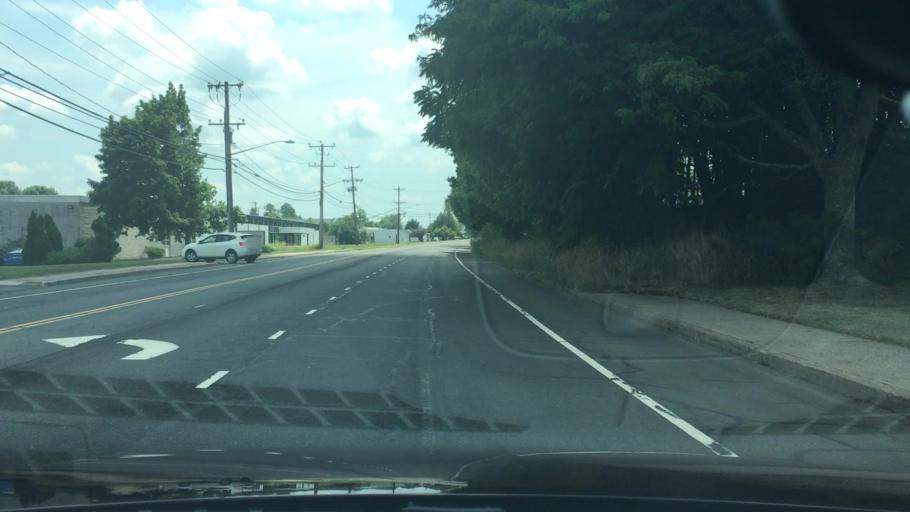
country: US
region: Connecticut
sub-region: Hartford County
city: New Britain
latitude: 41.6582
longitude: -72.7536
